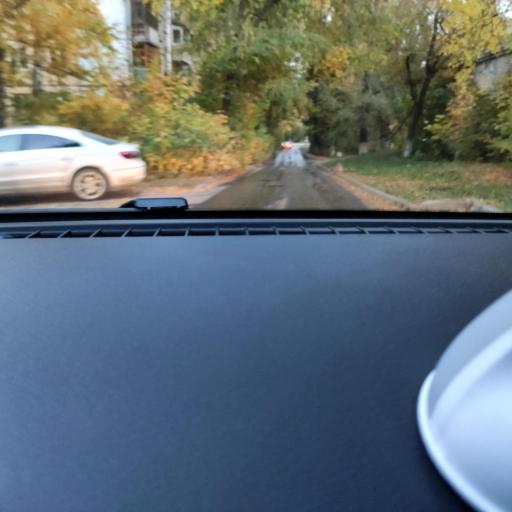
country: RU
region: Samara
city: Samara
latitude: 53.2301
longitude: 50.2184
